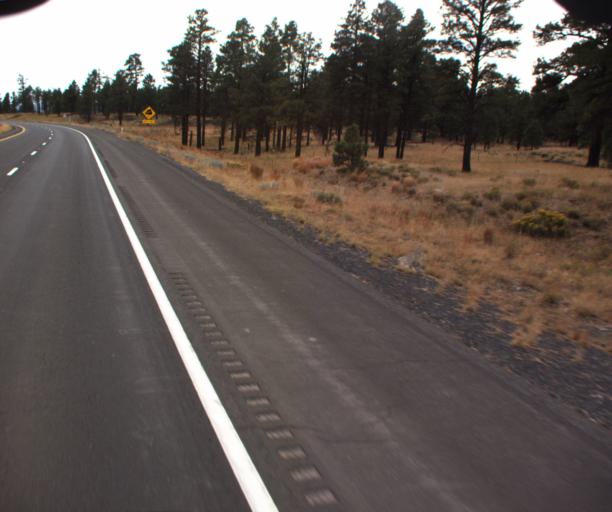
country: US
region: Arizona
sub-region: Coconino County
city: Flagstaff
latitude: 35.3537
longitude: -111.5695
